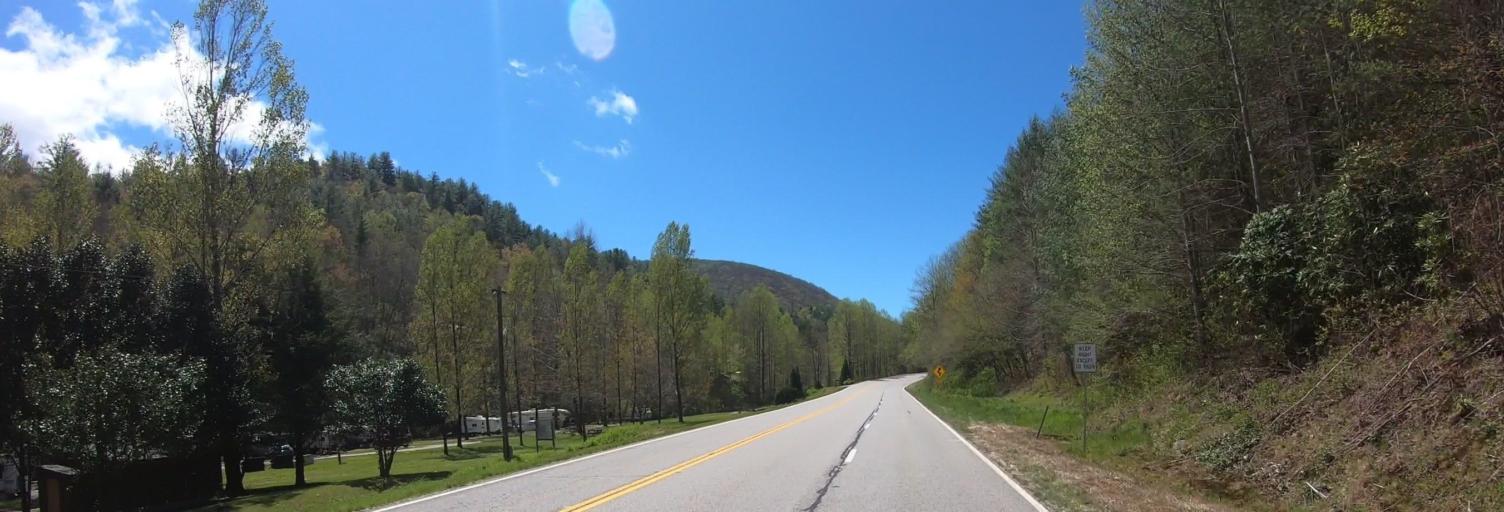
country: US
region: Georgia
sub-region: Towns County
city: Hiawassee
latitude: 34.8284
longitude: -83.7316
